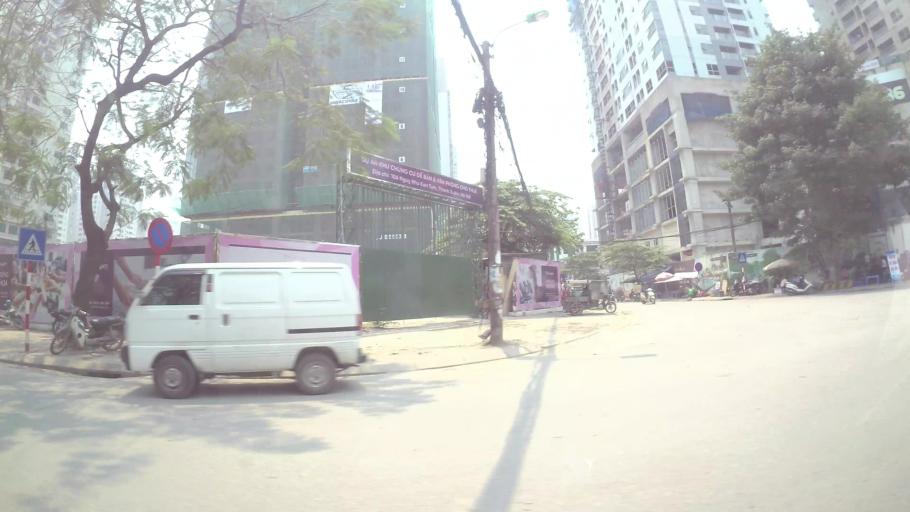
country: VN
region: Ha Noi
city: Thanh Xuan
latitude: 21.0013
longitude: 105.8037
